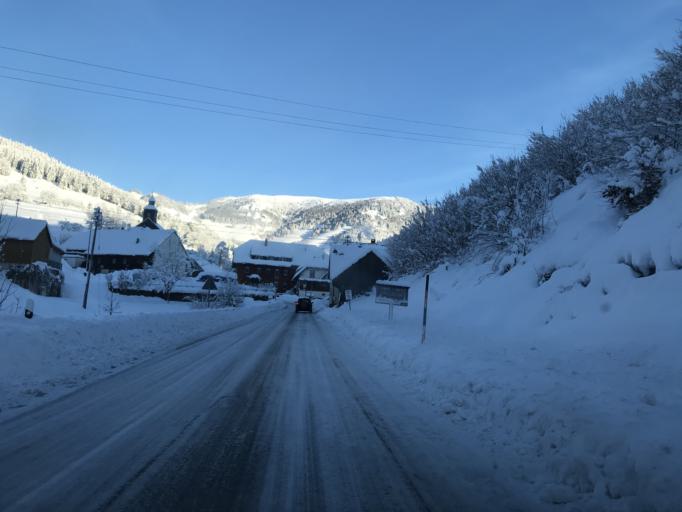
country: DE
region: Baden-Wuerttemberg
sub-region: Freiburg Region
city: Bollen
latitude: 47.7939
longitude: 7.8274
